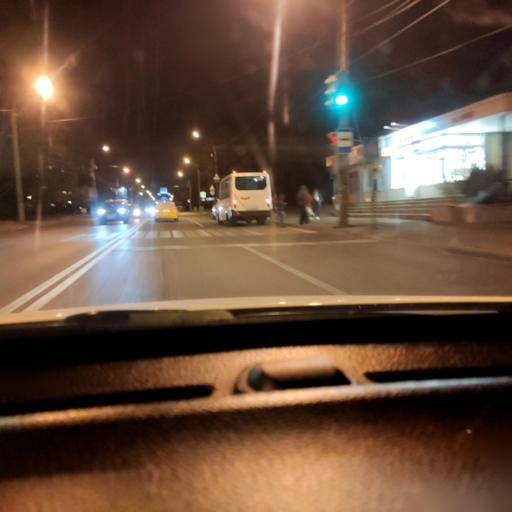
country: RU
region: Voronezj
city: Podgornoye
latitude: 51.7166
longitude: 39.1628
